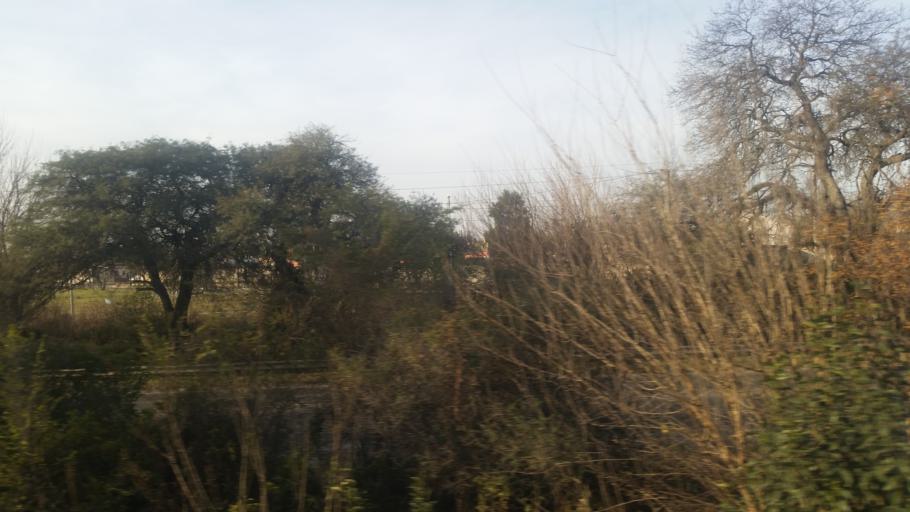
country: AR
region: Cordoba
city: Malvinas Argentinas
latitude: -31.4791
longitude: -64.0887
